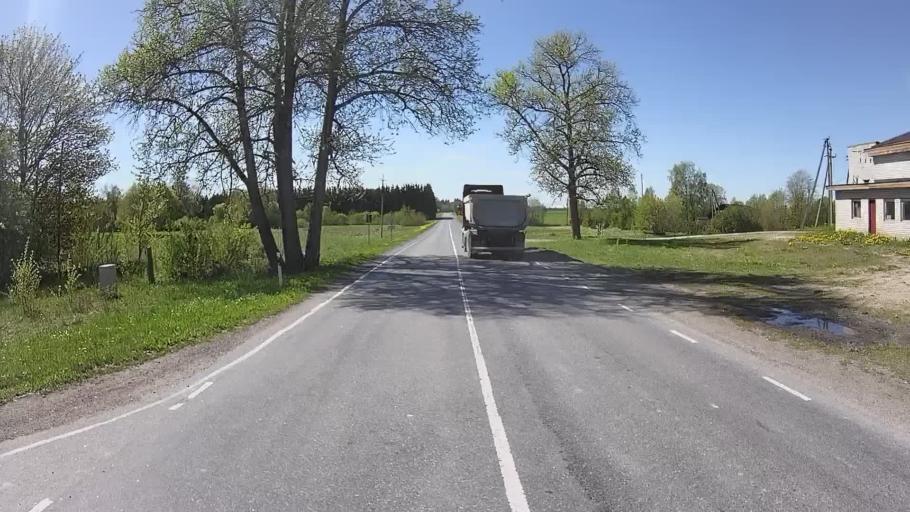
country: EE
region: Raplamaa
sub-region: Kehtna vald
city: Kehtna
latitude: 59.0456
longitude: 25.1155
